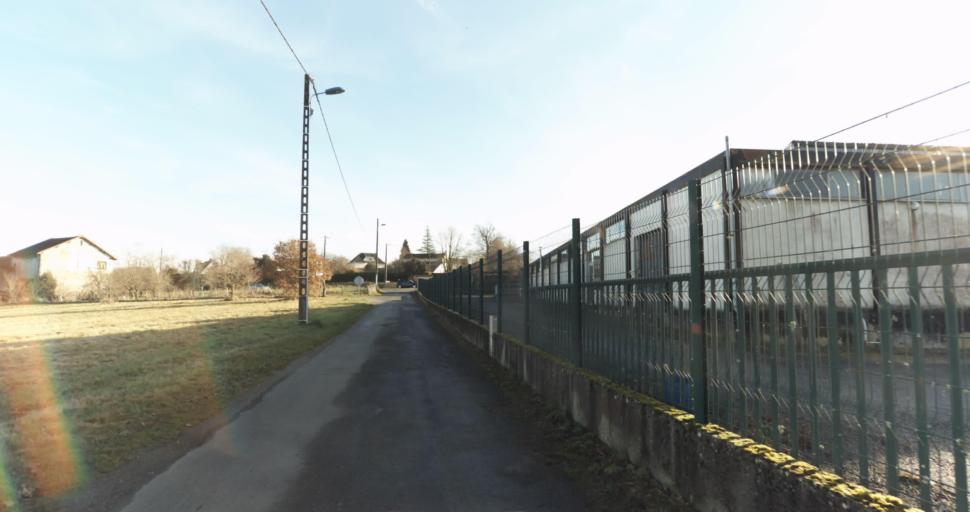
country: FR
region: Limousin
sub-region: Departement de la Haute-Vienne
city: Aixe-sur-Vienne
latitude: 45.7973
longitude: 1.1167
